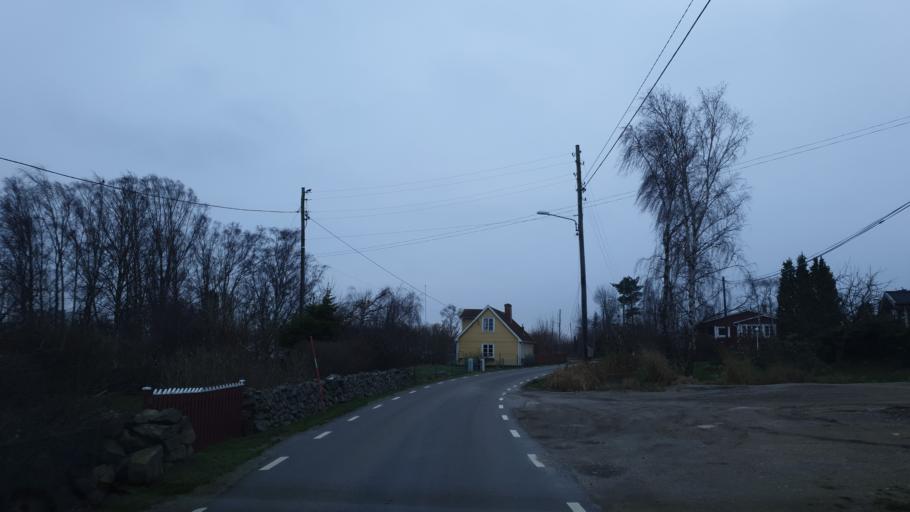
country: SE
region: Blekinge
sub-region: Karlskrona Kommun
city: Karlskrona
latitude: 56.1247
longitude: 15.6256
